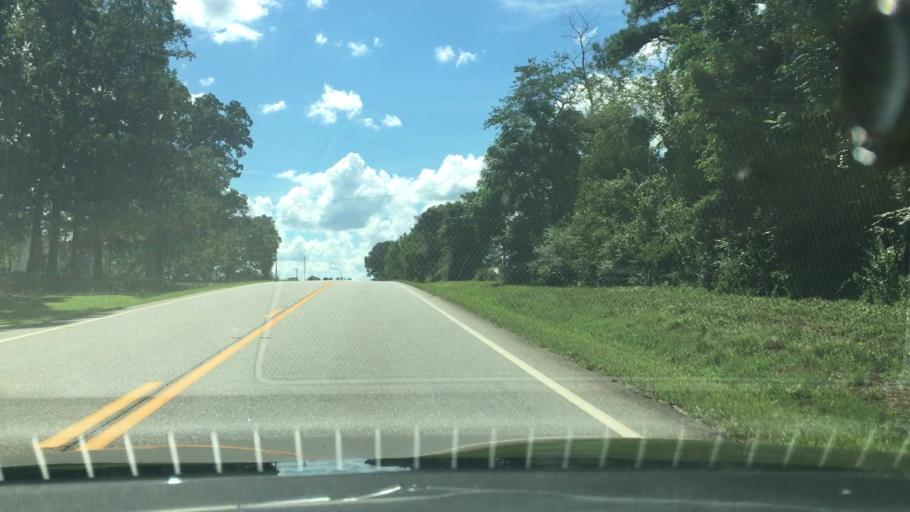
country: US
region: Georgia
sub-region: Jasper County
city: Monticello
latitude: 33.3005
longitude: -83.7167
